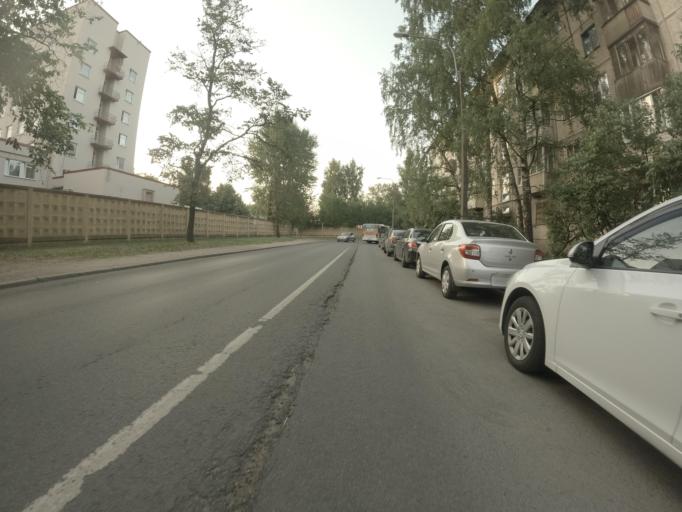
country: RU
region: Leningrad
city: Kalininskiy
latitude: 59.9853
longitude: 30.4121
